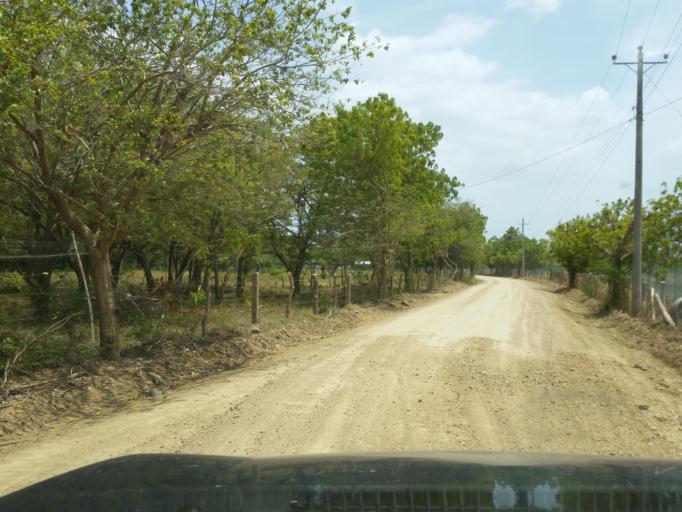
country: NI
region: Rivas
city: Tola
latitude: 11.4212
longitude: -86.0354
